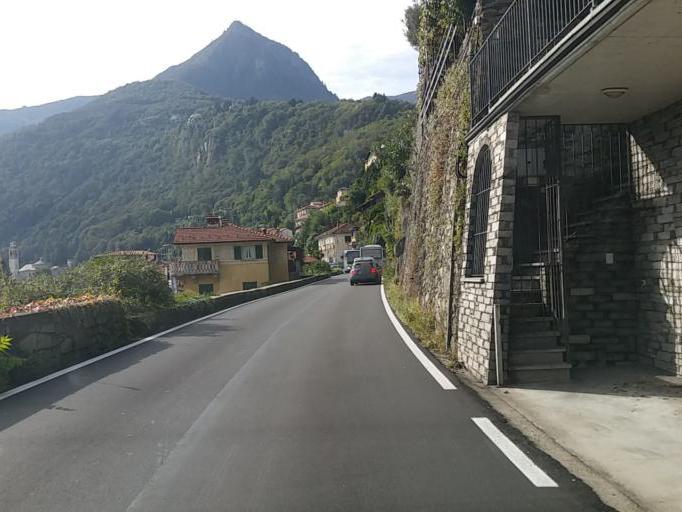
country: IT
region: Piedmont
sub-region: Provincia Verbano-Cusio-Ossola
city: Cannero Riviera
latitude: 46.0232
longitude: 8.6866
